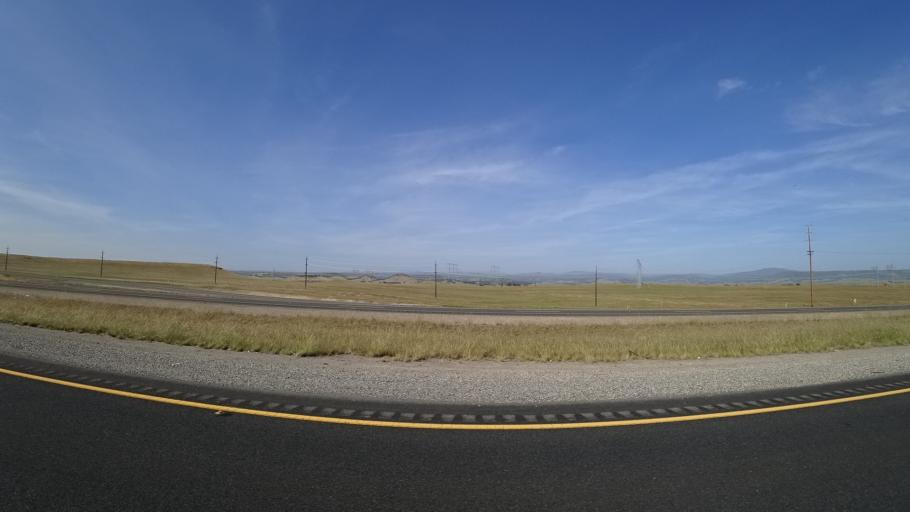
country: US
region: California
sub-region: Butte County
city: Durham
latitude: 39.6187
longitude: -121.6881
